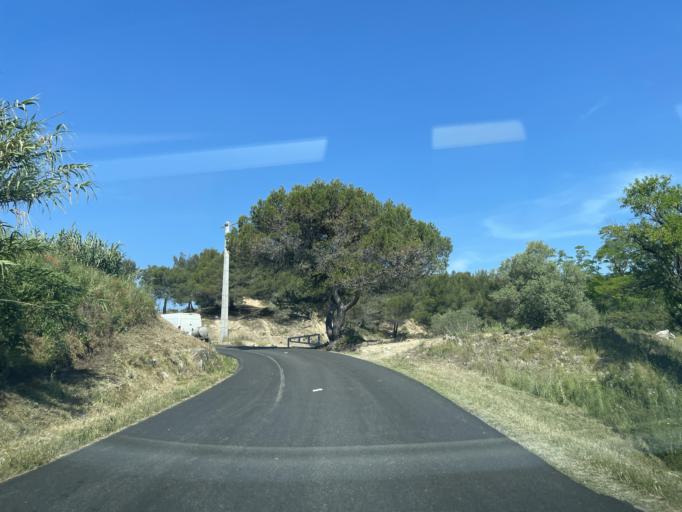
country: FR
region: Provence-Alpes-Cote d'Azur
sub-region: Departement des Bouches-du-Rhone
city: Saint-Mitre-les-Remparts
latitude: 43.4486
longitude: 5.0277
